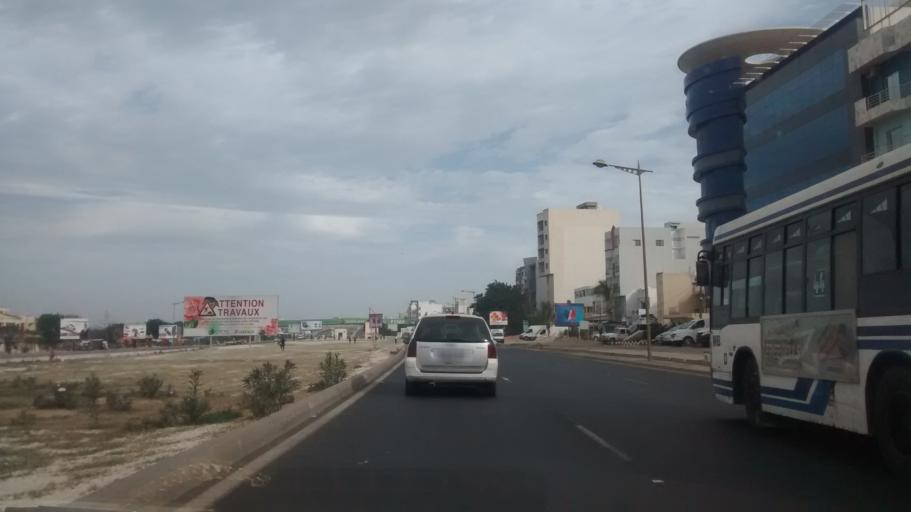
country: SN
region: Dakar
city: Mermoz Boabab
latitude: 14.7241
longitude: -17.4710
